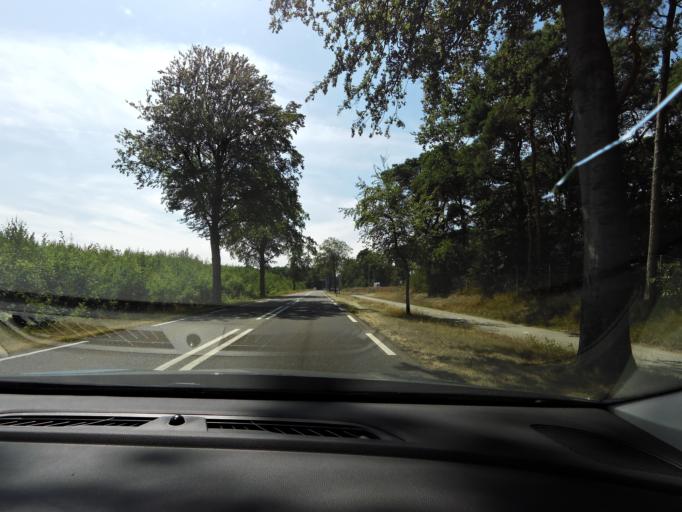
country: NL
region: Limburg
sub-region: Gemeente Leudal
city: Heythuysen
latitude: 51.1973
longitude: 5.8880
